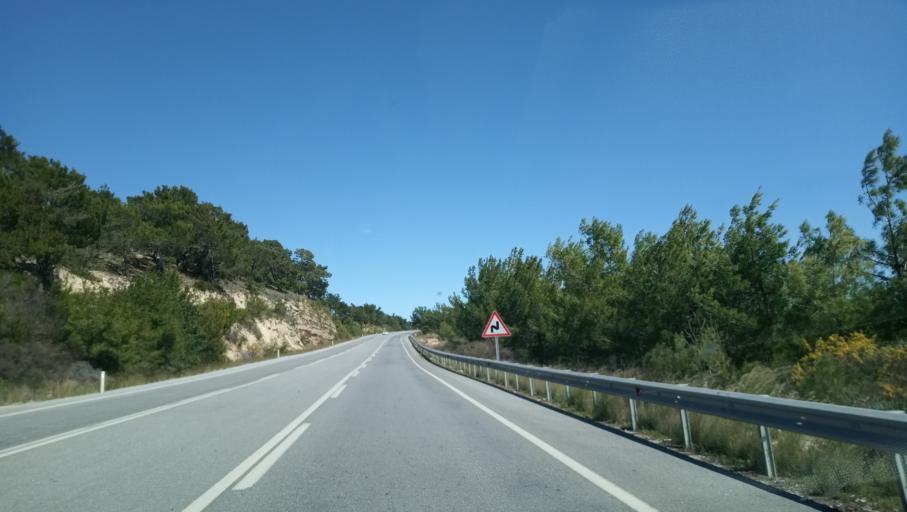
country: TR
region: Antalya
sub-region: Manavgat
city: Kizilagac
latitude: 36.7535
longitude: 31.6259
